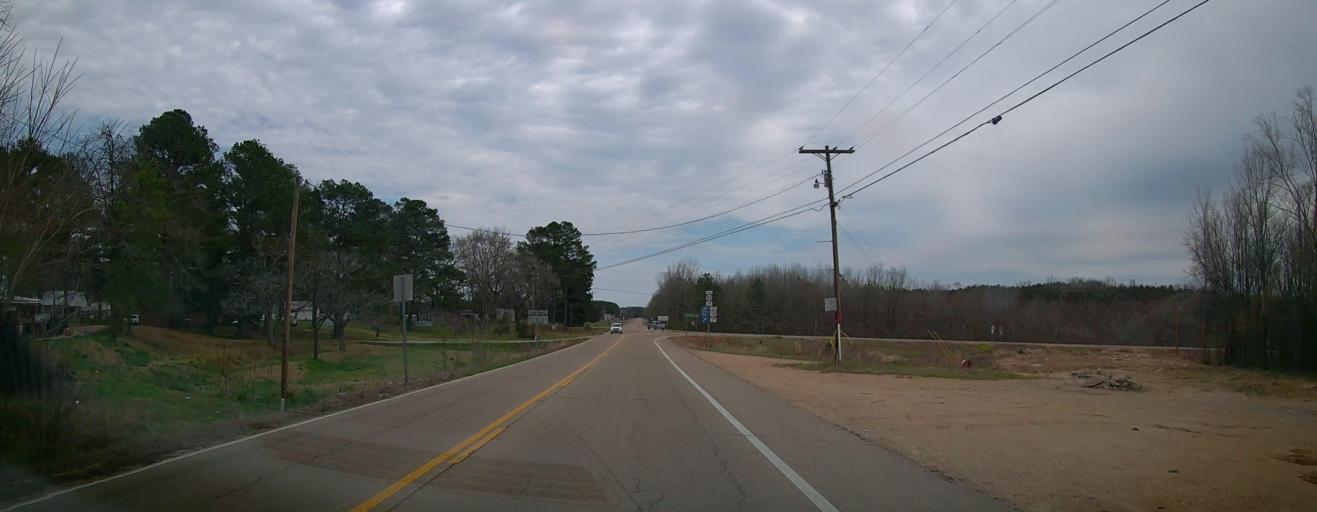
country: US
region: Mississippi
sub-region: Itawamba County
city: Fulton
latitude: 34.2344
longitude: -88.2578
